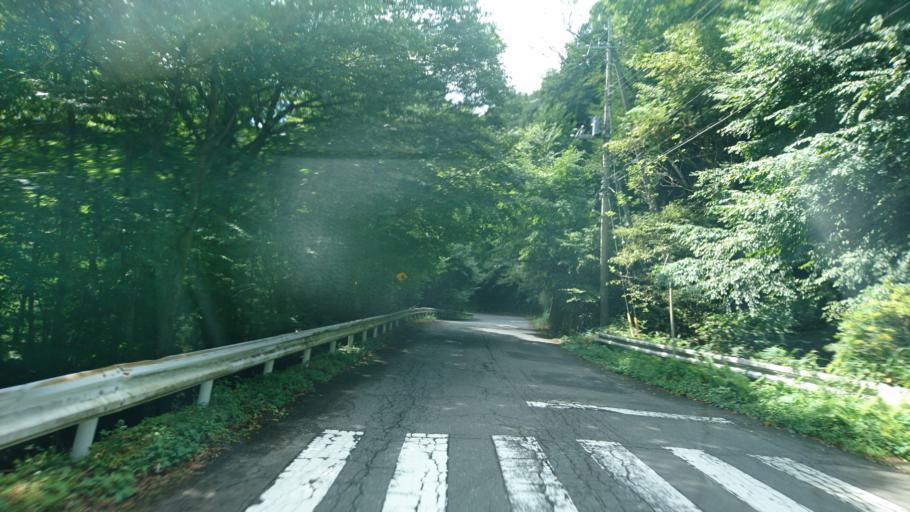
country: JP
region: Gunma
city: Omamacho-omama
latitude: 36.6080
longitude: 139.2353
